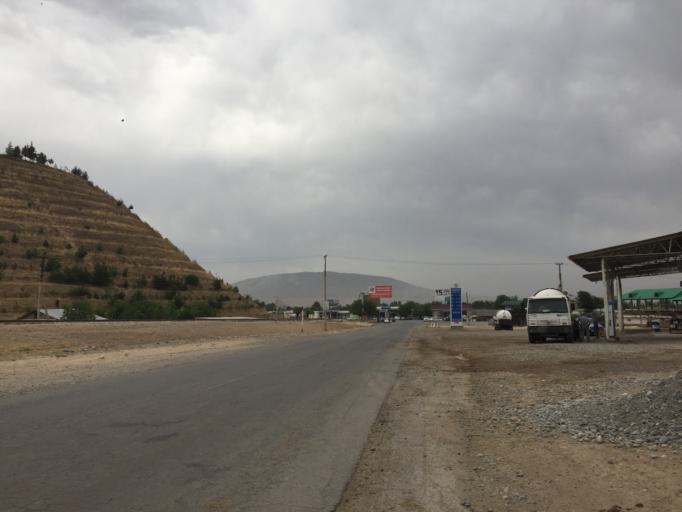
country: TJ
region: Khatlon
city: Moskva
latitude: 37.7436
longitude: 69.4944
